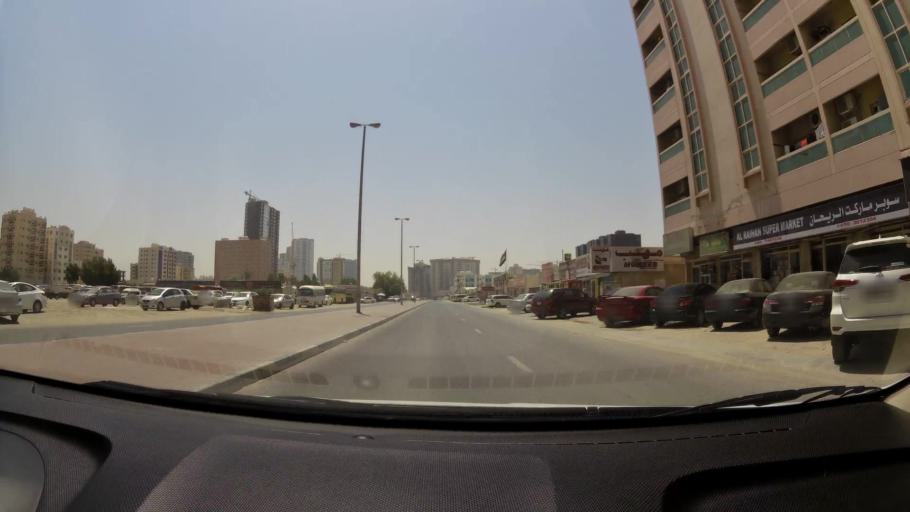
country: AE
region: Ajman
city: Ajman
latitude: 25.3927
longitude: 55.4587
